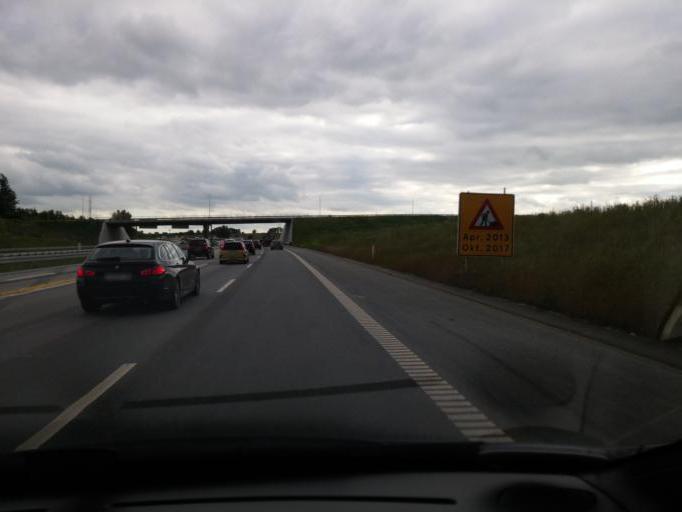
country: DK
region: Zealand
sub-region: Solrod Kommune
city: Solrod
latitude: 55.5375
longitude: 12.2015
